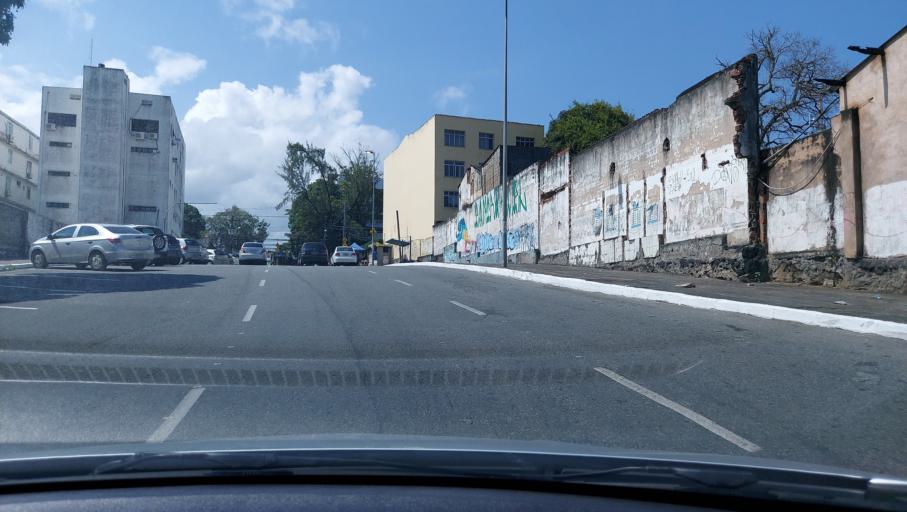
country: BR
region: Bahia
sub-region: Salvador
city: Salvador
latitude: -12.9664
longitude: -38.4715
